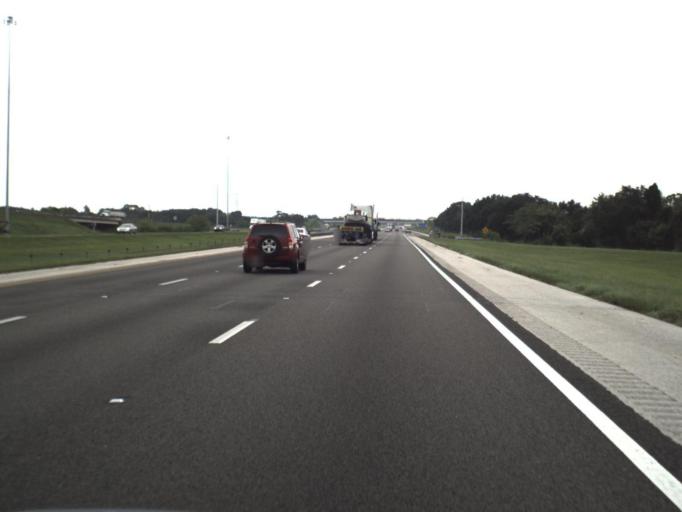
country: US
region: Florida
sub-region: Manatee County
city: Ellenton
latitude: 27.5825
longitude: -82.5149
